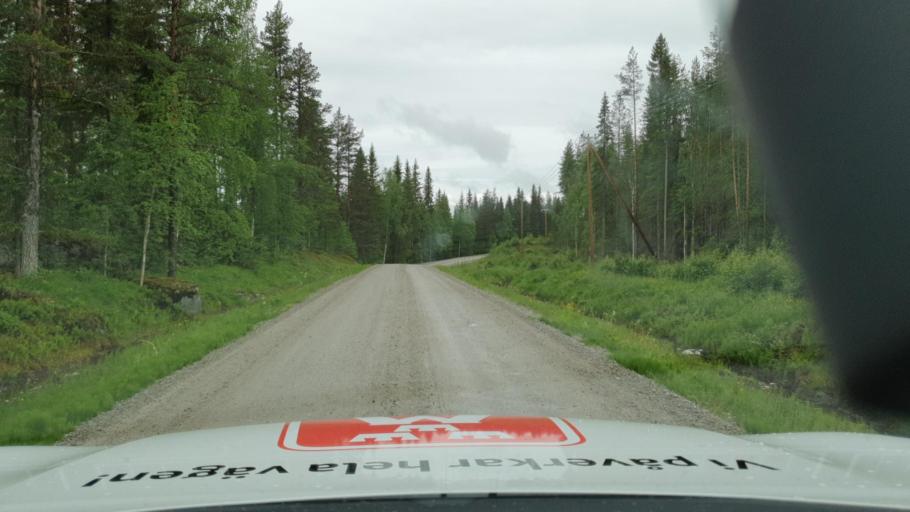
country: SE
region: Vaesterbotten
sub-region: Asele Kommun
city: Asele
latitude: 63.9717
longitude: 17.0556
